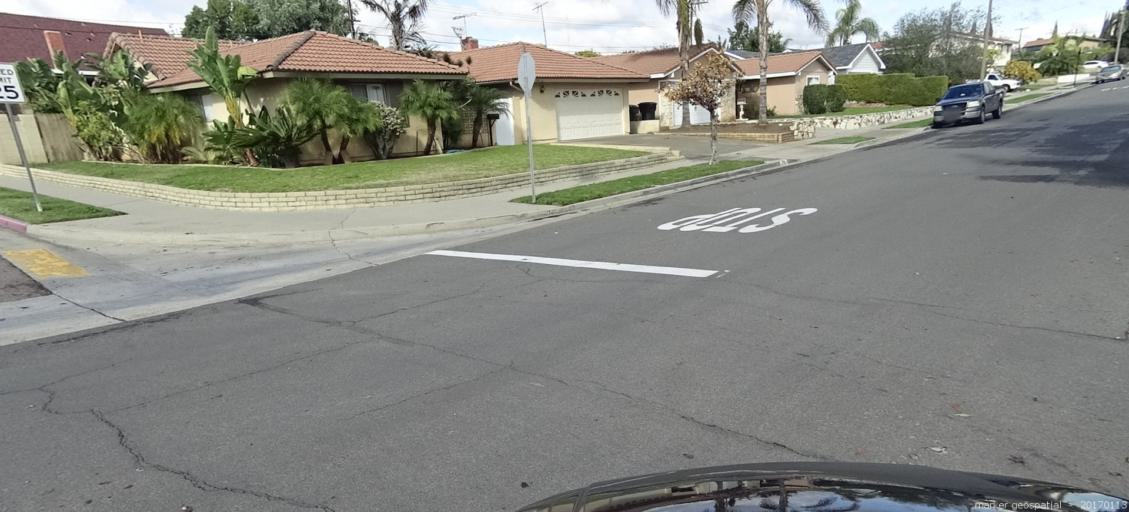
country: US
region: California
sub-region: Orange County
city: Placentia
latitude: 33.8934
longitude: -117.8500
